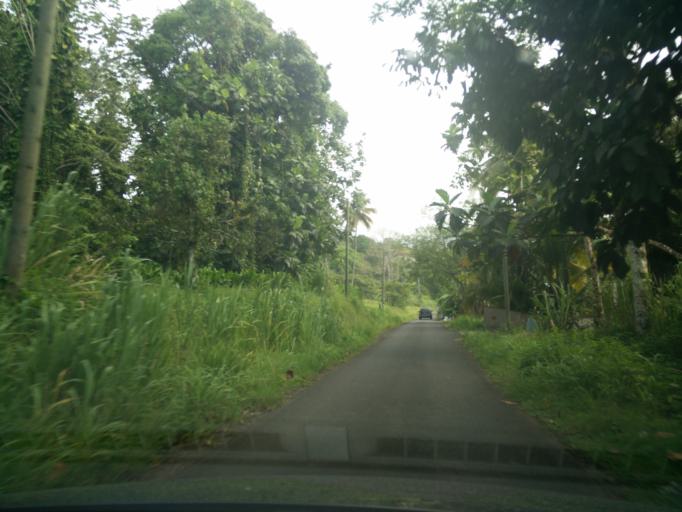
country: GP
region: Guadeloupe
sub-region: Guadeloupe
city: Petit-Bourg
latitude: 16.1144
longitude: -61.5972
